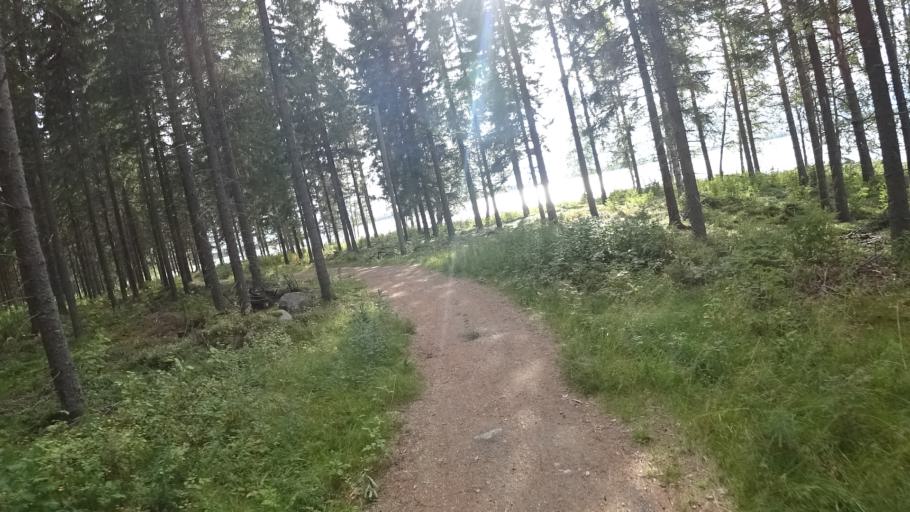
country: FI
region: North Karelia
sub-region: Joensuu
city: Ilomantsi
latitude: 62.6705
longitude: 30.9069
